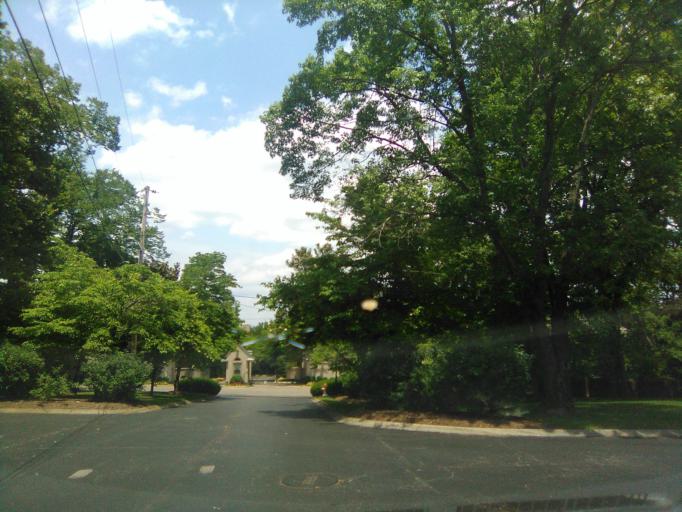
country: US
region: Tennessee
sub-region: Davidson County
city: Belle Meade
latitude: 36.1259
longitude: -86.8298
